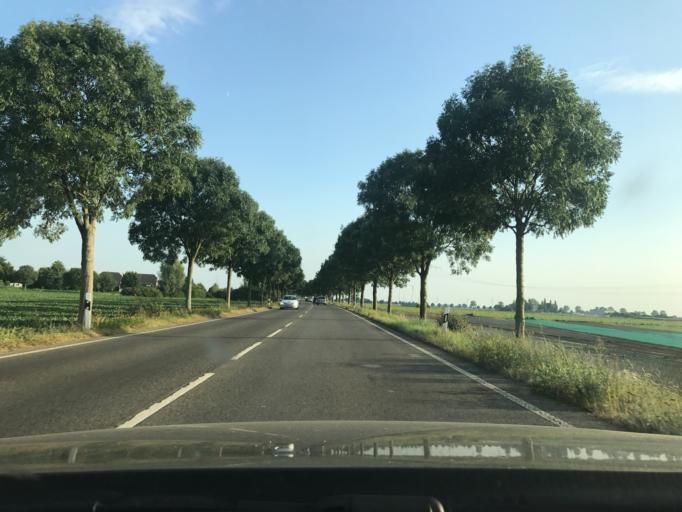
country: DE
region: North Rhine-Westphalia
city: Tonisvorst
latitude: 51.3787
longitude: 6.4897
